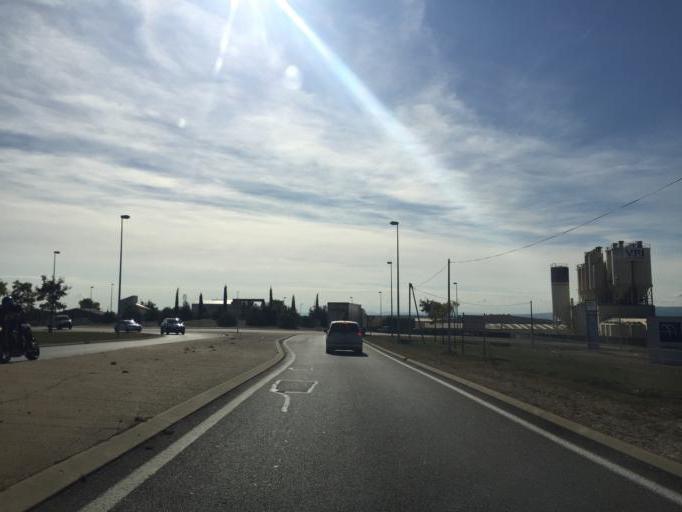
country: FR
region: Rhone-Alpes
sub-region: Departement de la Drome
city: Malataverne
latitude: 44.4633
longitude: 4.7590
